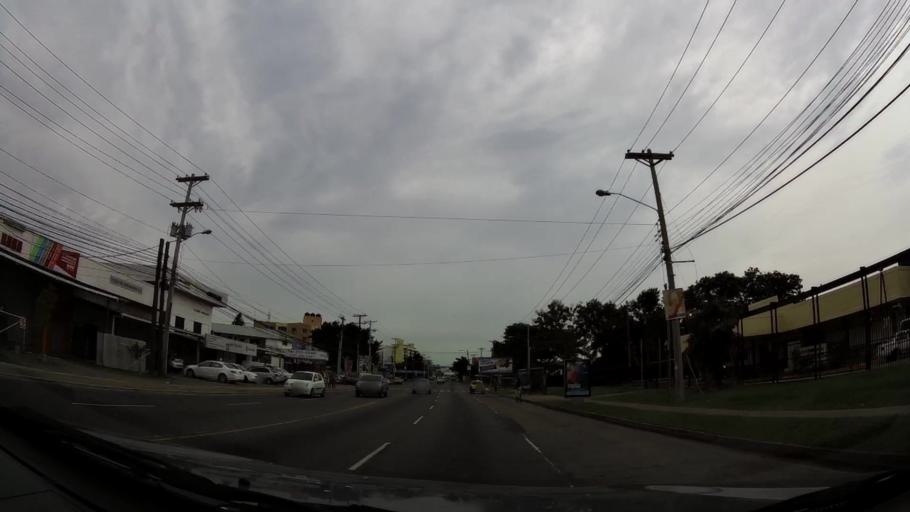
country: PA
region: Panama
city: San Miguelito
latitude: 9.0373
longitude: -79.4675
